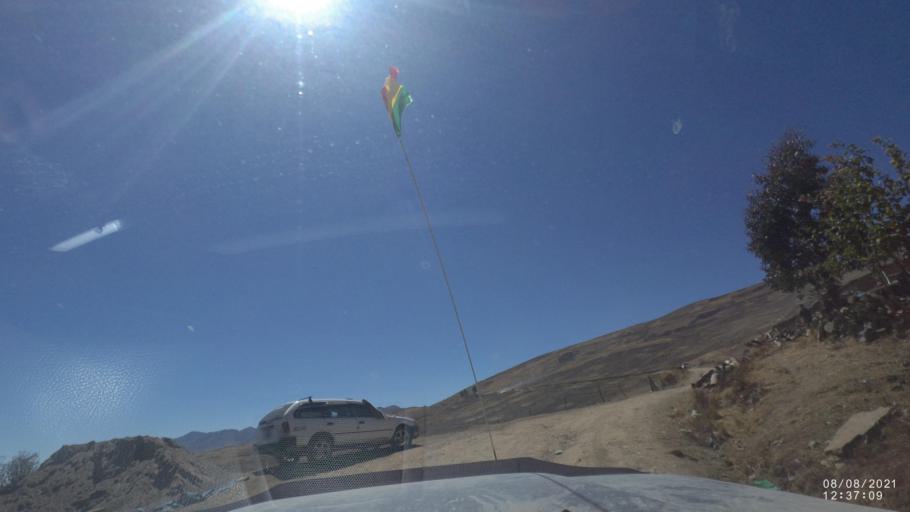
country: BO
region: Cochabamba
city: Colchani
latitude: -16.8385
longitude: -66.6281
